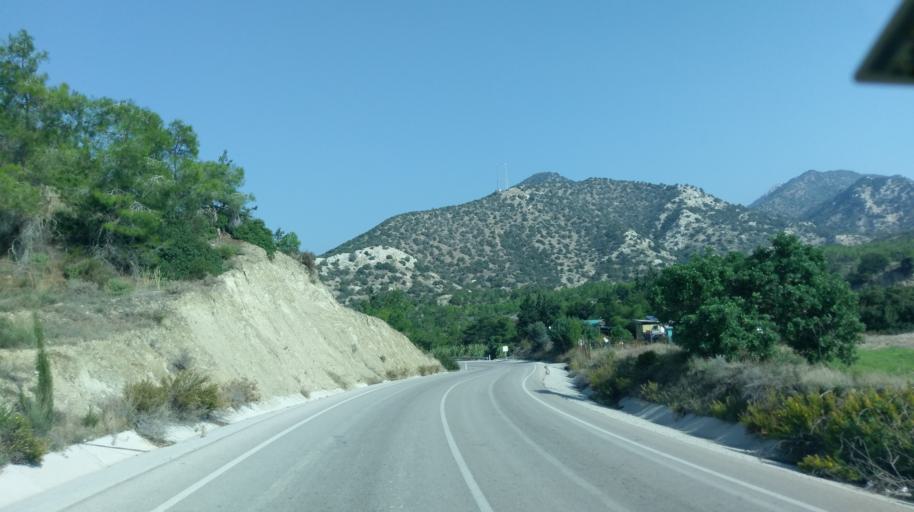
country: CY
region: Ammochostos
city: Lefkonoiko
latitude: 35.3419
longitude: 33.7119
